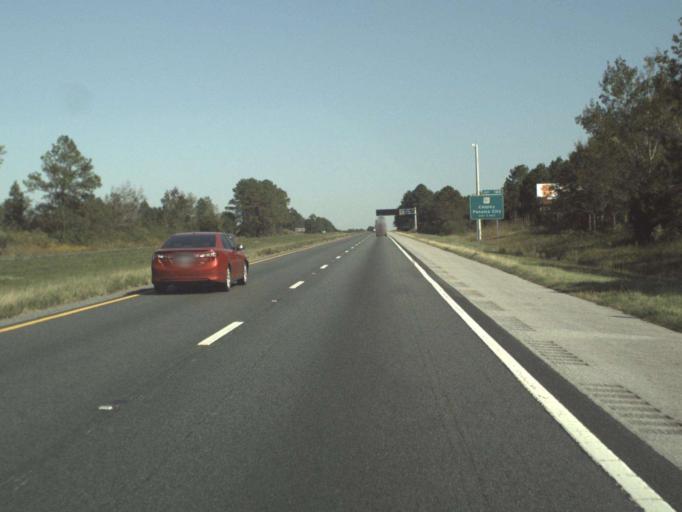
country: US
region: Florida
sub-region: Washington County
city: Chipley
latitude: 30.7511
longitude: -85.5749
